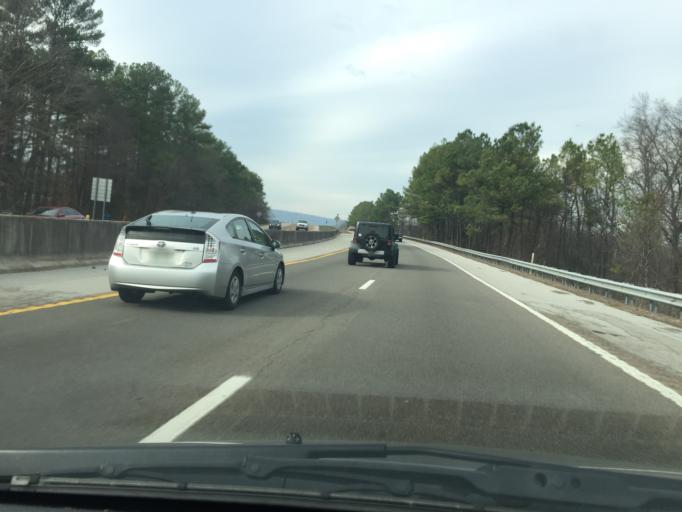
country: US
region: Tennessee
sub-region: Hamilton County
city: East Chattanooga
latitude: 35.1147
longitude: -85.2307
